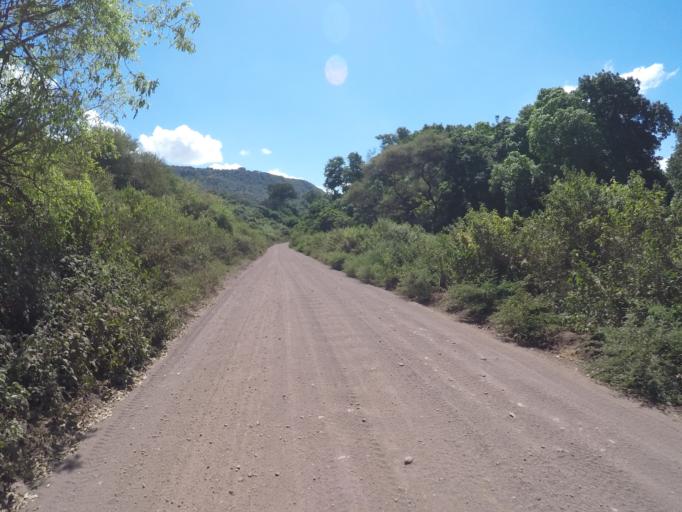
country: TZ
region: Arusha
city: Mto wa Mbu
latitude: -3.3854
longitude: 35.8279
